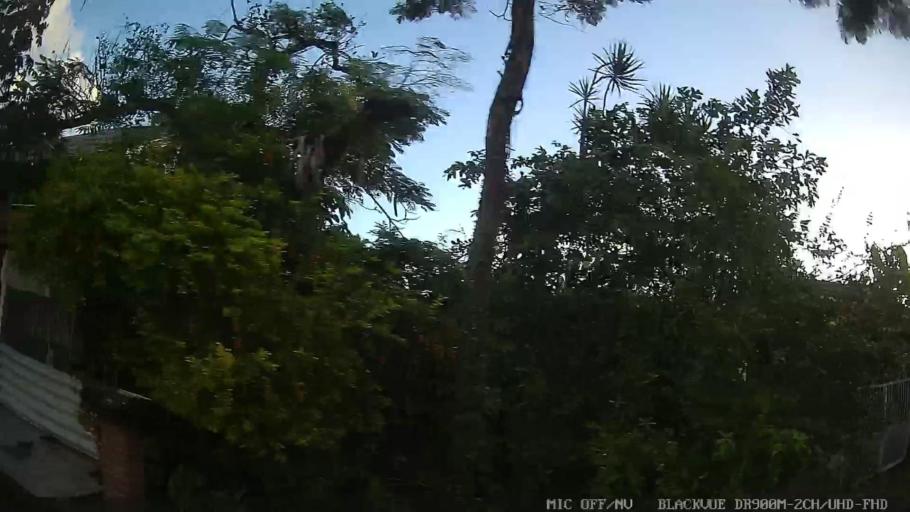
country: BR
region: Sao Paulo
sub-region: Itanhaem
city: Itanhaem
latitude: -24.1455
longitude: -46.7280
